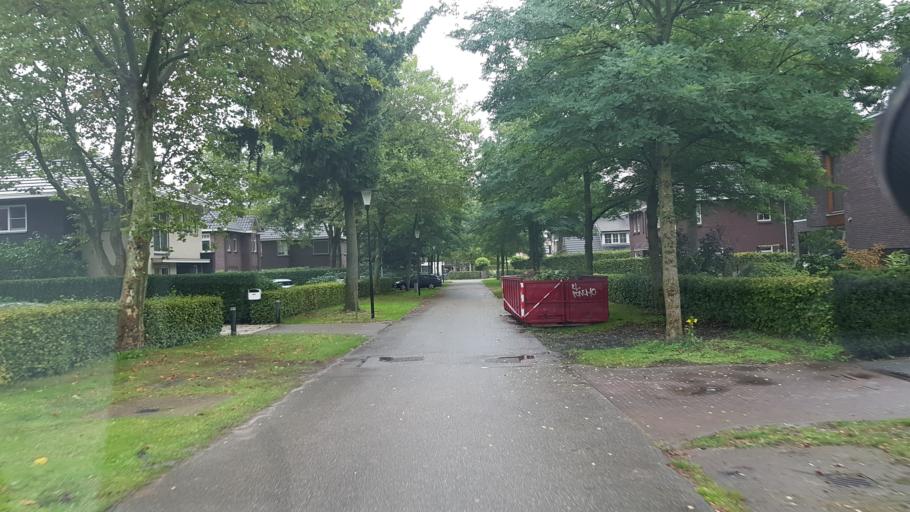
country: NL
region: Gelderland
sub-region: Gemeente Apeldoorn
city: Beekbergen
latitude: 52.1867
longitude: 5.9263
